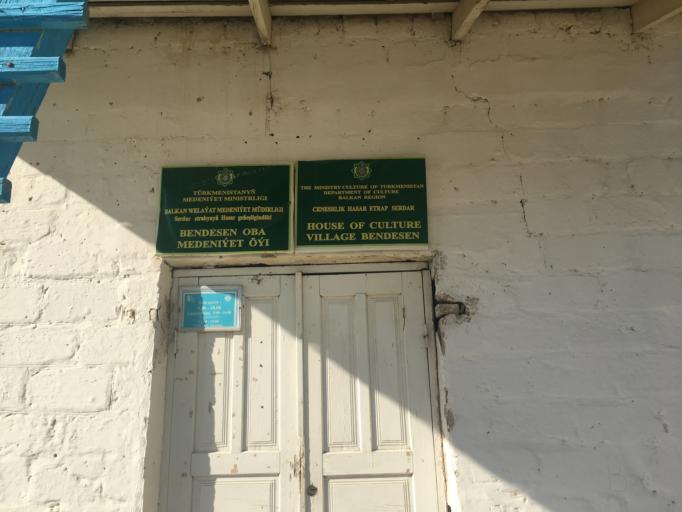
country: TM
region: Balkan
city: Magtymguly
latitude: 38.6341
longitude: 56.6088
